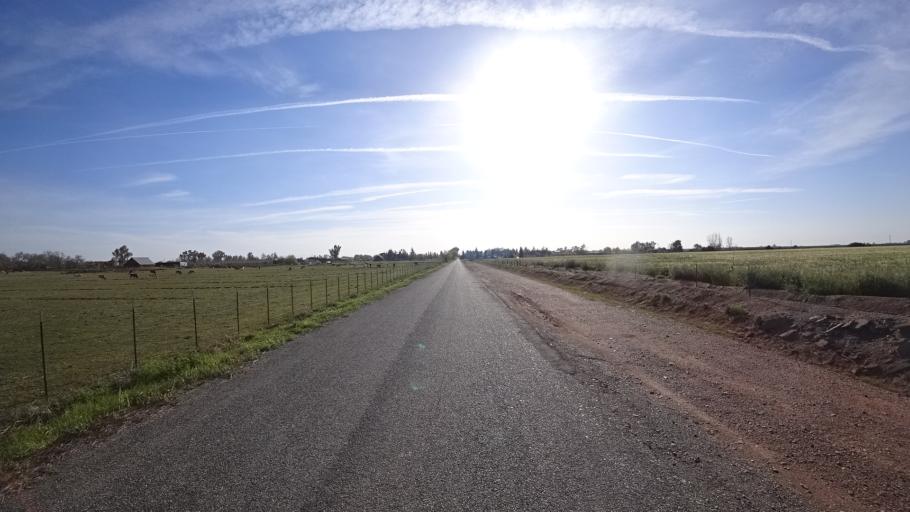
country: US
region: California
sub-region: Glenn County
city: Orland
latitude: 39.7154
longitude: -122.2332
